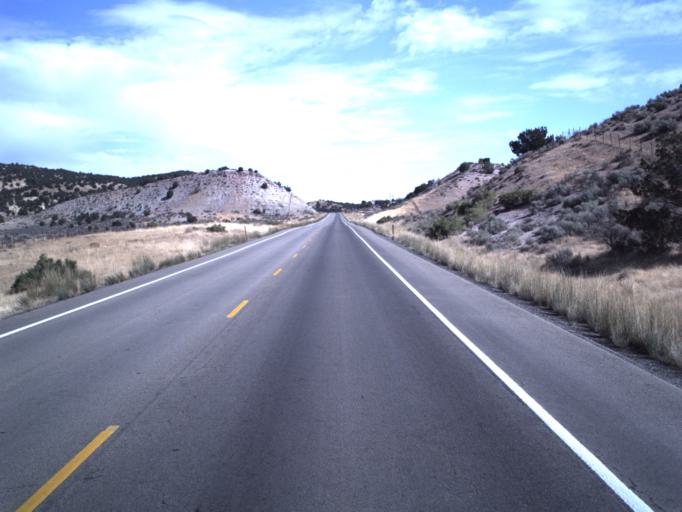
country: US
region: Utah
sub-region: Sanpete County
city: Gunnison
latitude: 39.3709
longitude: -111.9289
